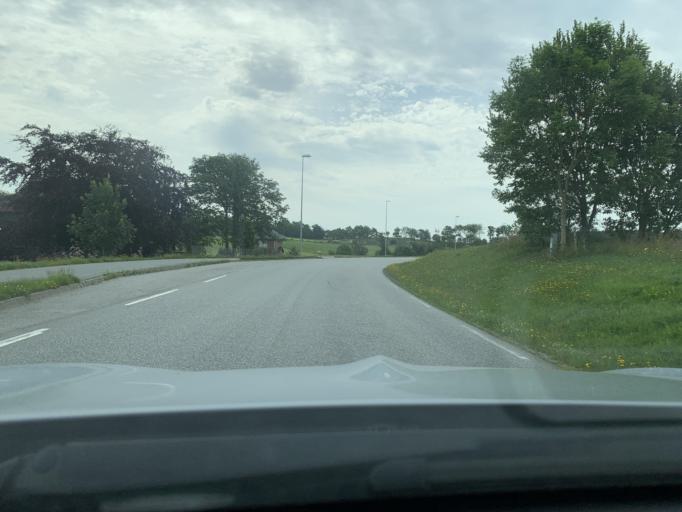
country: NO
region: Rogaland
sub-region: Time
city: Bryne
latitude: 58.7585
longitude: 5.7093
